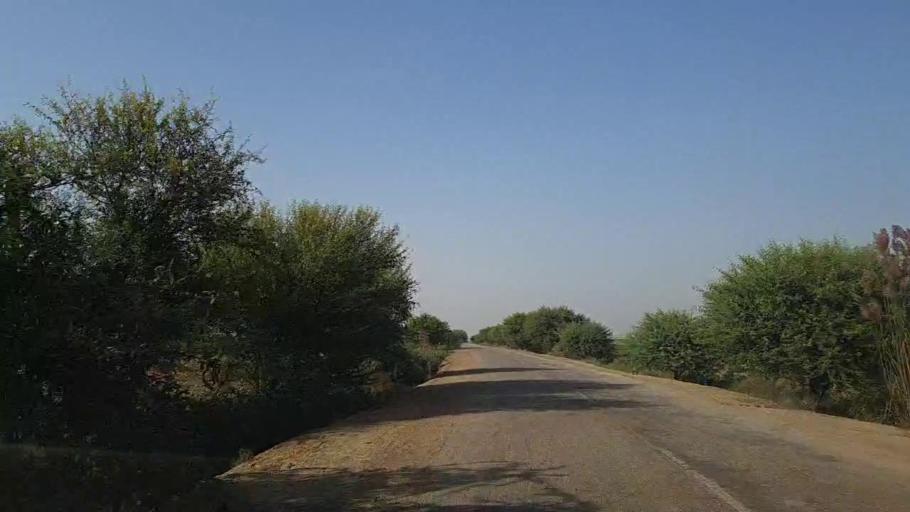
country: PK
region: Sindh
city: Mirpur Batoro
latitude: 24.5772
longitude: 68.3949
